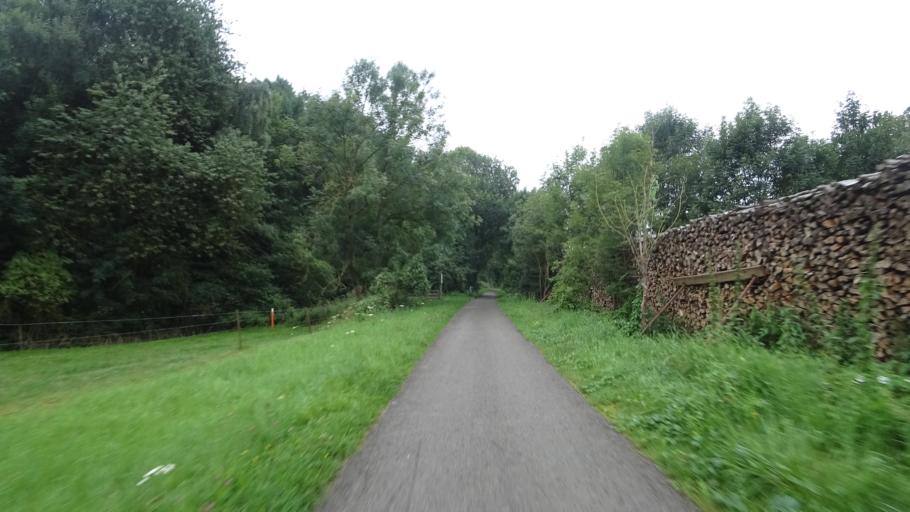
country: BE
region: Wallonia
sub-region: Province de Namur
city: Namur
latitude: 50.4973
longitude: 4.8658
